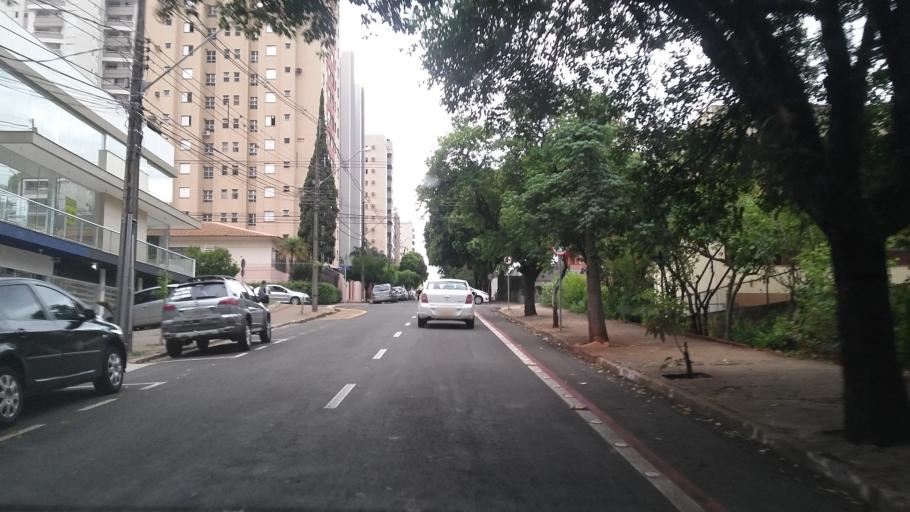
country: BR
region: Parana
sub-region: Londrina
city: Londrina
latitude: -23.3177
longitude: -51.1698
